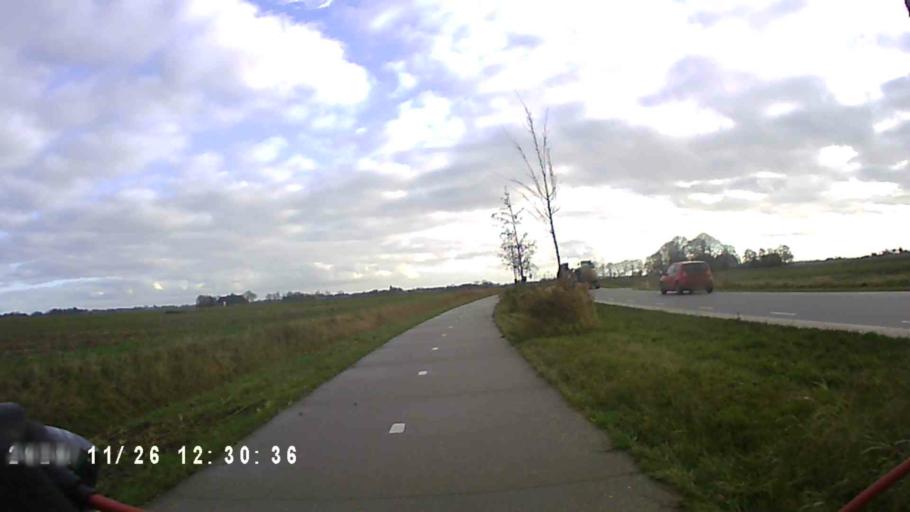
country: NL
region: Groningen
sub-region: Gemeente Bedum
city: Bedum
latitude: 53.3278
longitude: 6.7126
